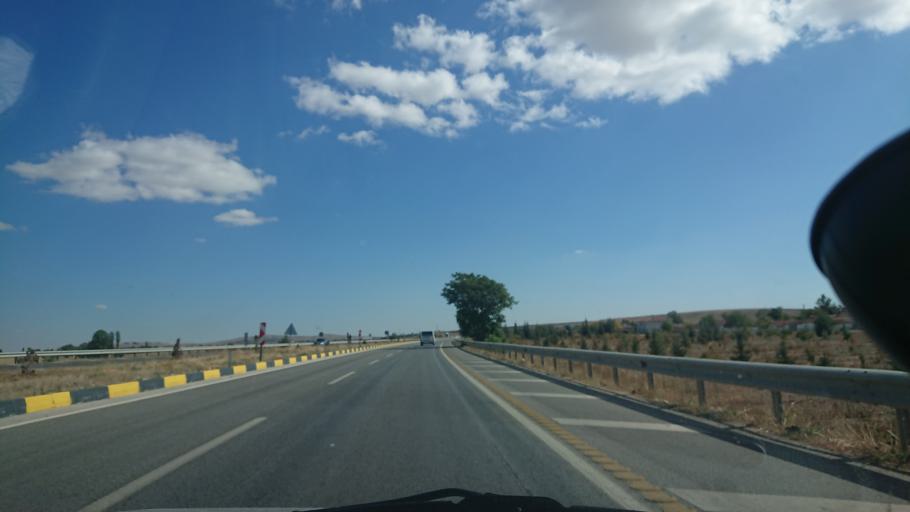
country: TR
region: Eskisehir
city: Mahmudiye
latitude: 39.5372
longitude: 30.9434
